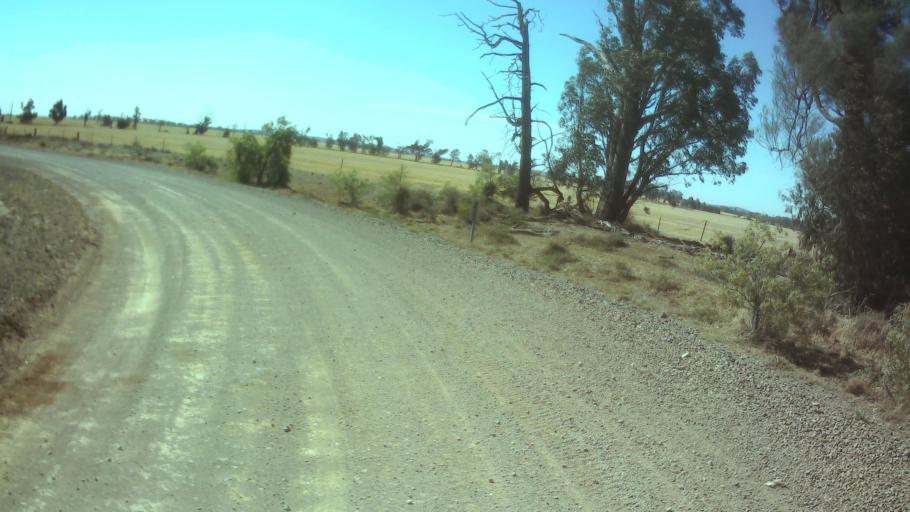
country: AU
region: New South Wales
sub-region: Forbes
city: Forbes
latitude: -33.7053
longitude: 147.7467
